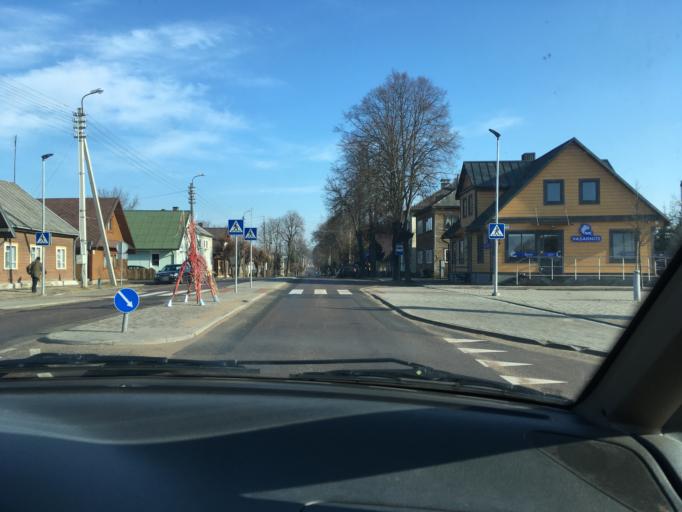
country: LT
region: Panevezys
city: Rokiskis
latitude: 55.7467
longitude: 25.8402
